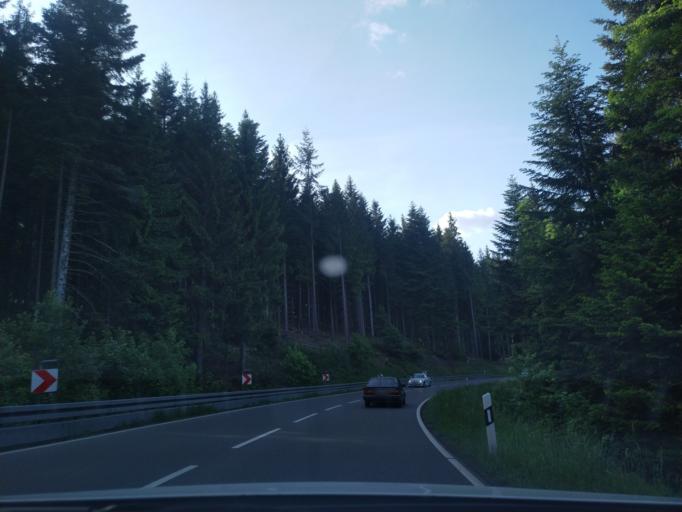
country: DE
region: Baden-Wuerttemberg
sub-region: Karlsruhe Region
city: Lossburg
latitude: 48.4301
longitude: 8.4408
